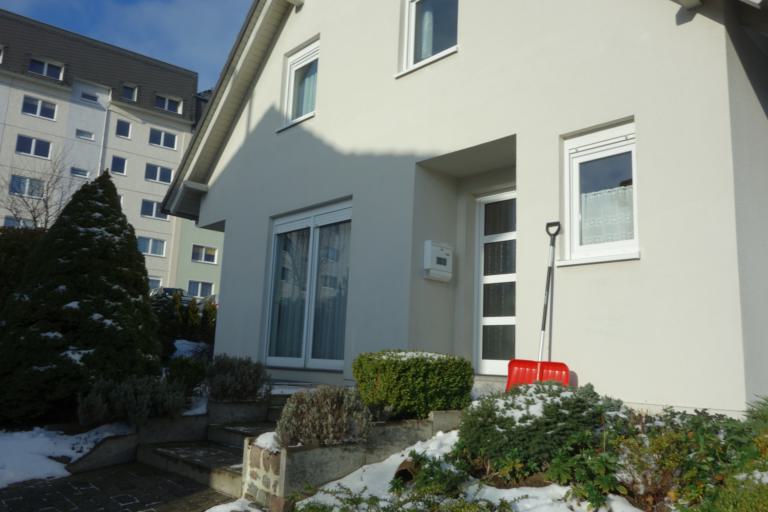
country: DE
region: Saxony
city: Freiberg
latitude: 50.9202
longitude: 13.3292
